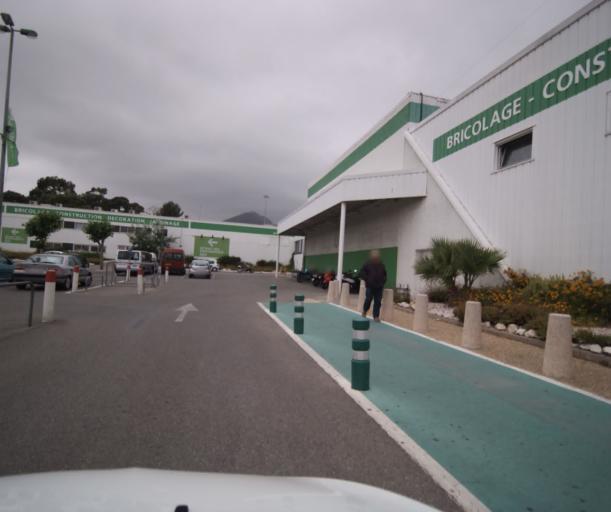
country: FR
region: Provence-Alpes-Cote d'Azur
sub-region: Departement du Var
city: La Garde
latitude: 43.1399
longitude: 6.0035
